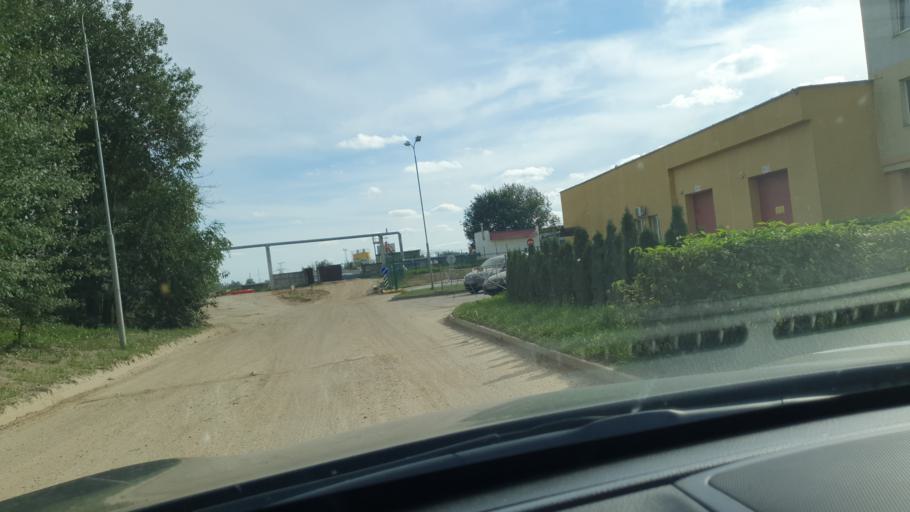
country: BY
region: Minsk
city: Azyartso
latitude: 53.8597
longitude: 27.4007
